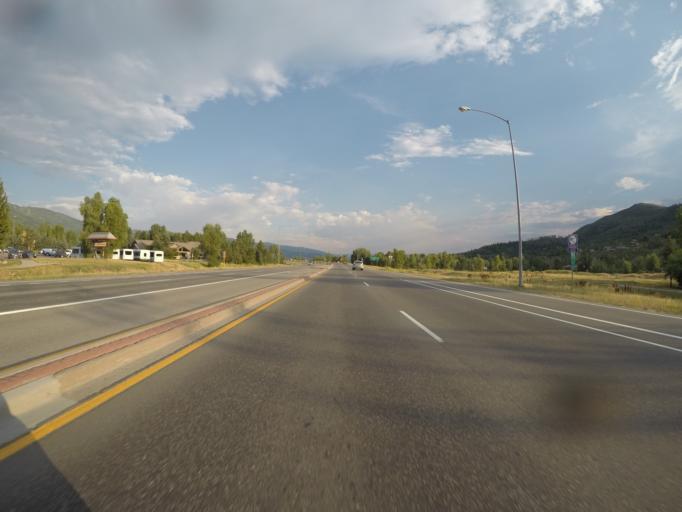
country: US
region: Colorado
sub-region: Routt County
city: Steamboat Springs
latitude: 40.4646
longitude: -106.8257
